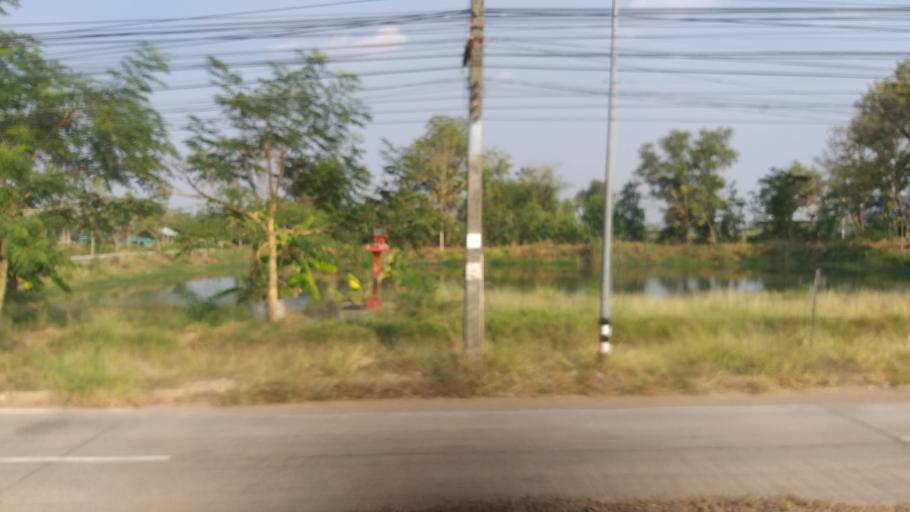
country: TH
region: Changwat Udon Thani
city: Non Sa-at
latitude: 16.9618
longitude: 102.8927
